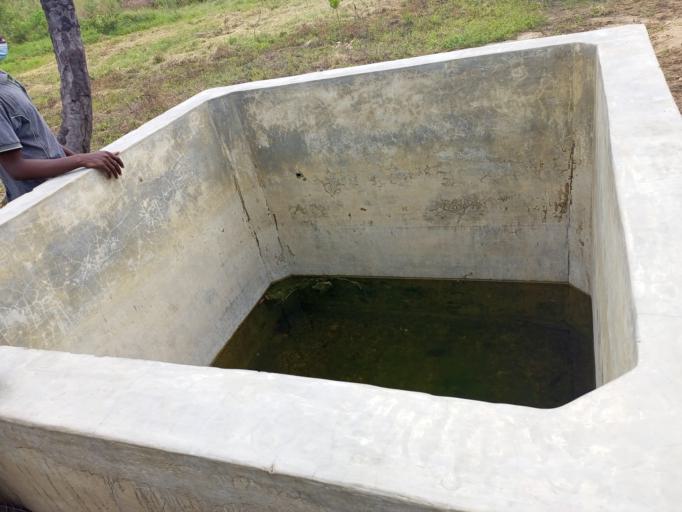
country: TG
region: Kara
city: Niamtougou
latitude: 9.6559
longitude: 0.9656
